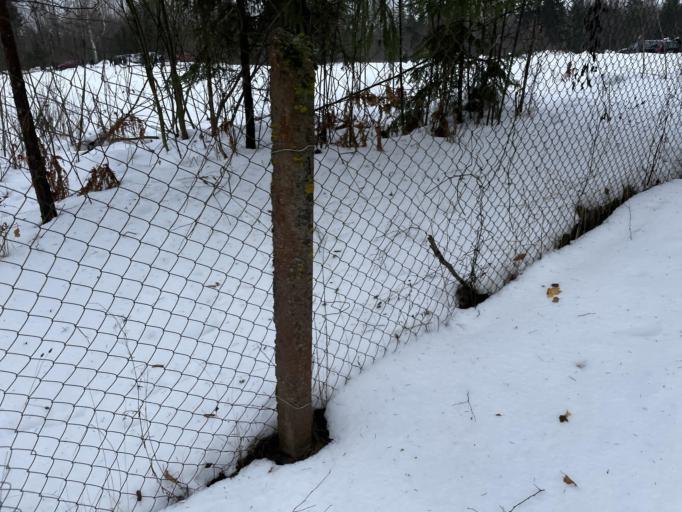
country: LV
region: Ludzas Rajons
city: Ludza
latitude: 56.4479
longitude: 27.6350
